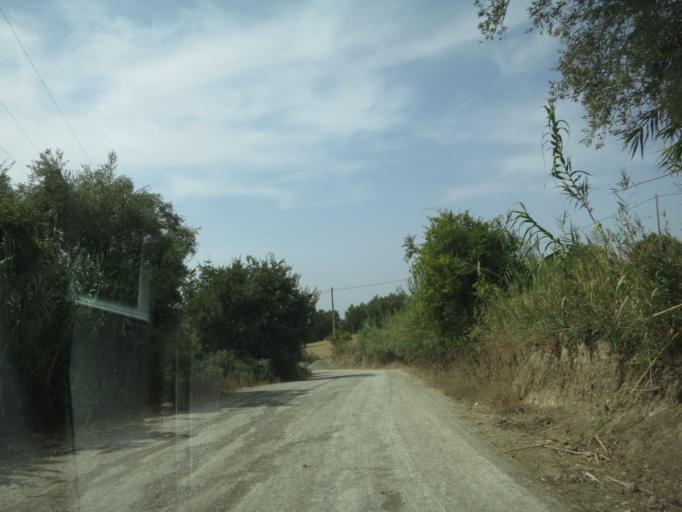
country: MA
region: Meknes-Tafilalet
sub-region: Meknes
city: Meknes
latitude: 34.0742
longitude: -5.5425
